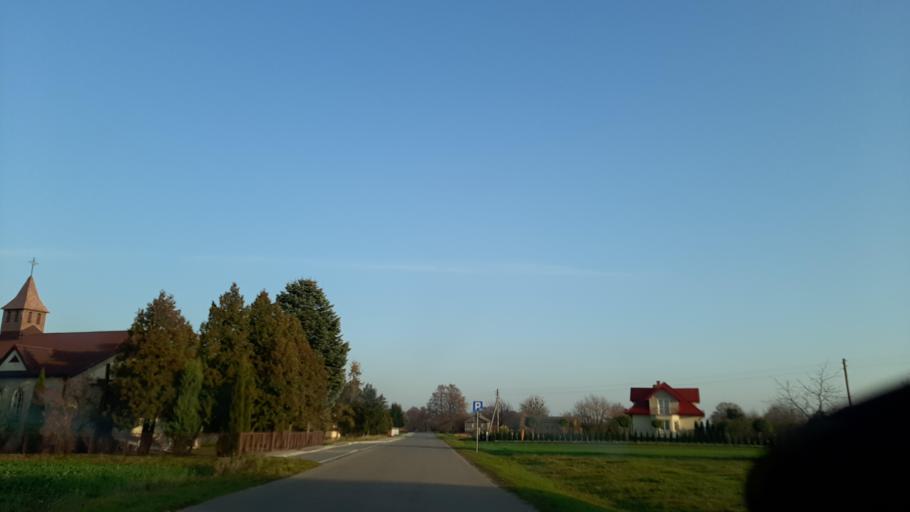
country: PL
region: Lublin Voivodeship
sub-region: Powiat lubelski
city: Garbow
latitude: 51.3847
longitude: 22.3728
